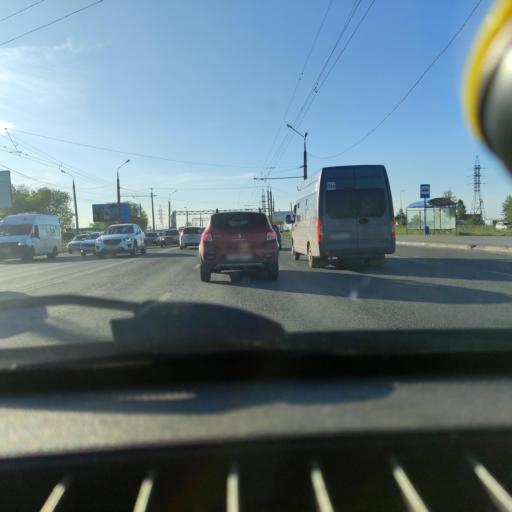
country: RU
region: Samara
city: Tol'yatti
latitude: 53.5437
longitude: 49.3849
